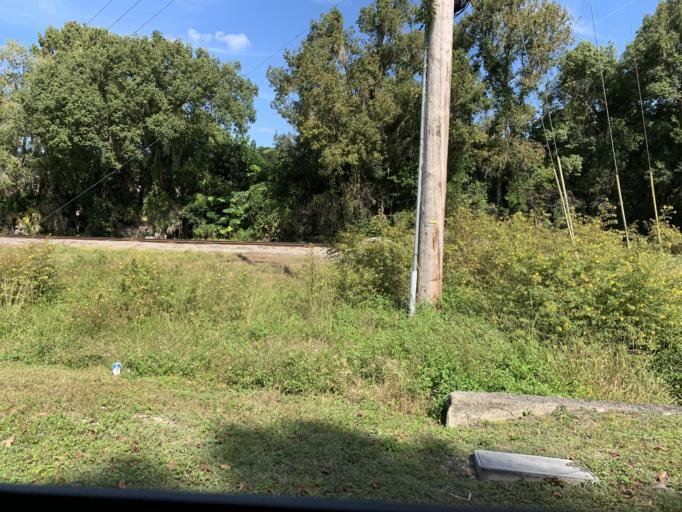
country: US
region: Florida
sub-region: Marion County
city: Ocala
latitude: 29.1754
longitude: -82.1337
